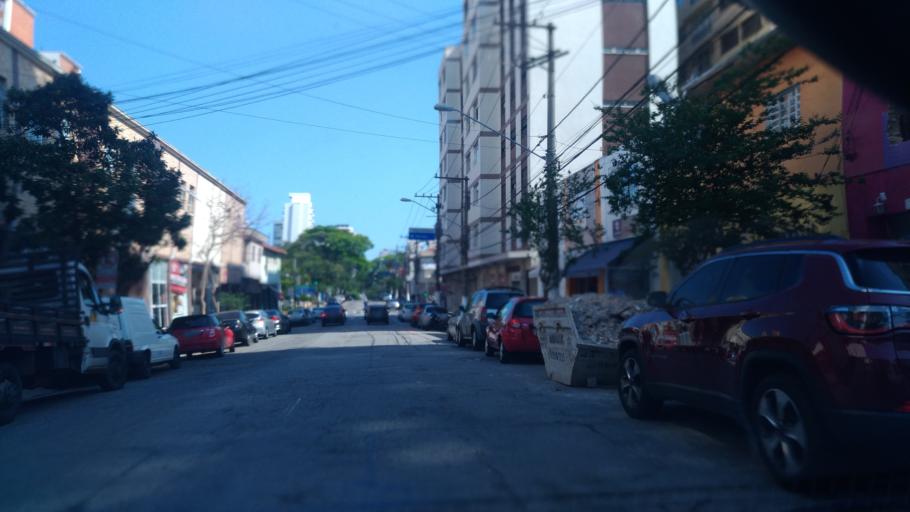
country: BR
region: Sao Paulo
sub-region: Sao Paulo
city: Sao Paulo
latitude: -23.5858
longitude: -46.6043
